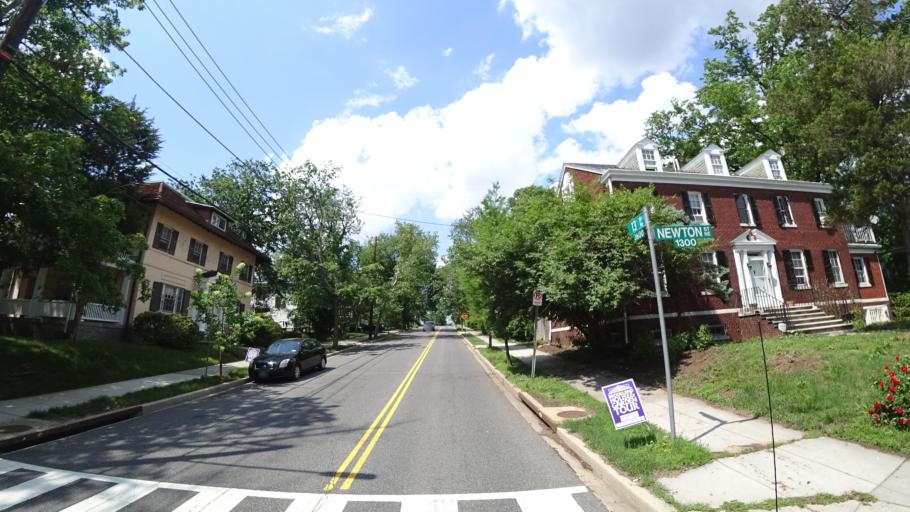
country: US
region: Maryland
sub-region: Prince George's County
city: Mount Rainier
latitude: 38.9337
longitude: -76.9888
